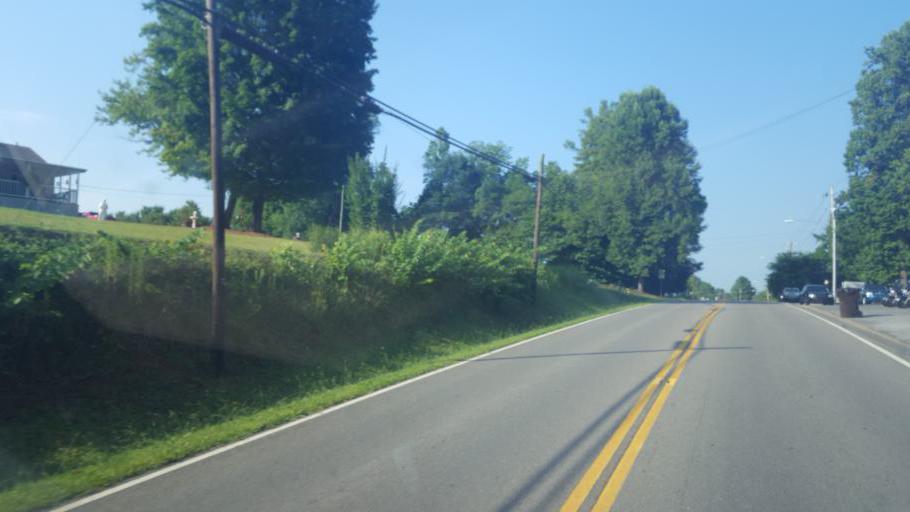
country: US
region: Tennessee
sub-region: Sullivan County
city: Bluff City
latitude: 36.4594
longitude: -82.2758
